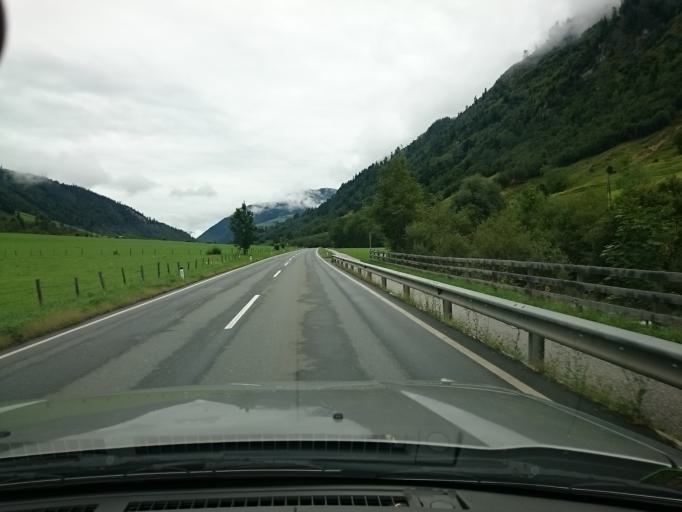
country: AT
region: Salzburg
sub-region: Politischer Bezirk Zell am See
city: Bruck an der Grossglocknerstrasse
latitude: 47.2451
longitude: 12.8271
